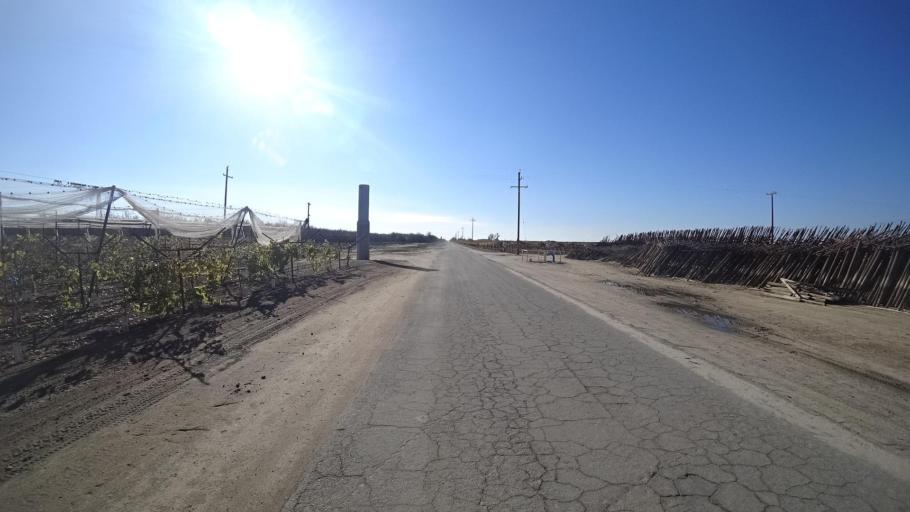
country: US
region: California
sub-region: Kern County
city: McFarland
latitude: 35.6964
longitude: -119.2674
